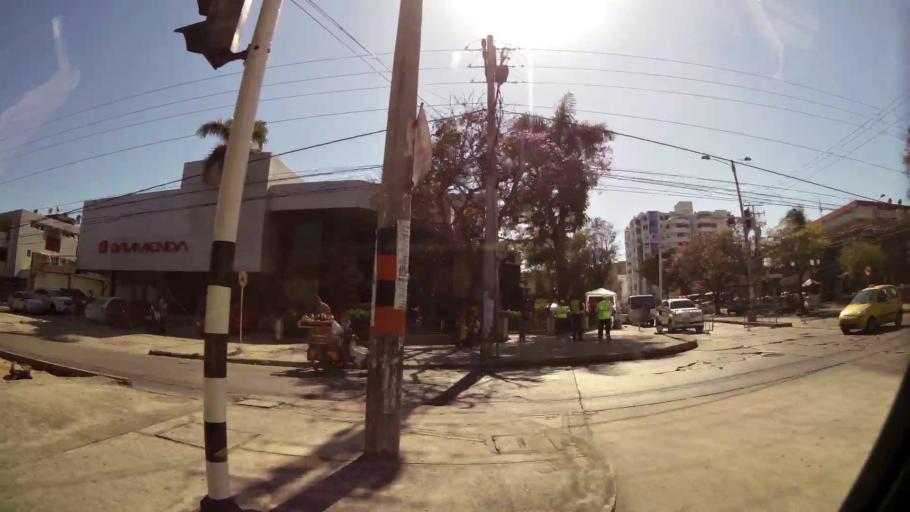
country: CO
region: Atlantico
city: Barranquilla
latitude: 10.9989
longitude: -74.8016
